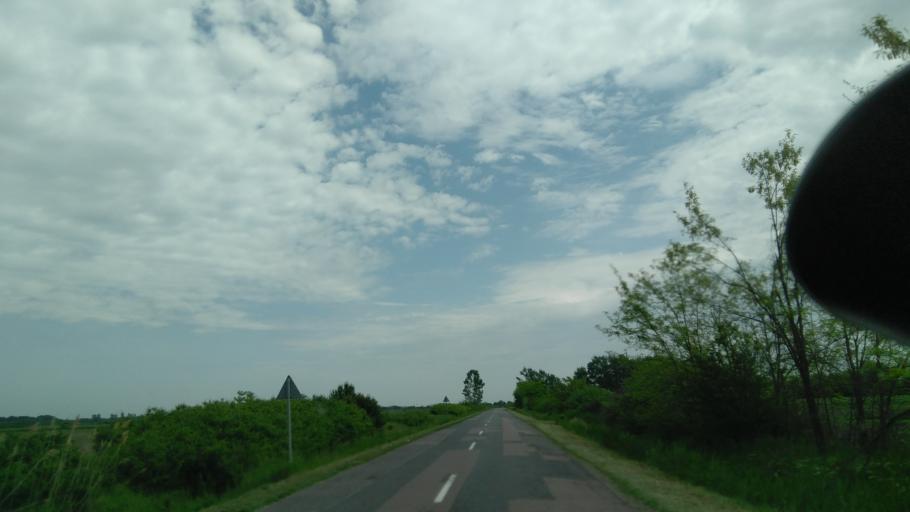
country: HU
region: Hajdu-Bihar
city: Komadi
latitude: 47.0233
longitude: 21.5666
